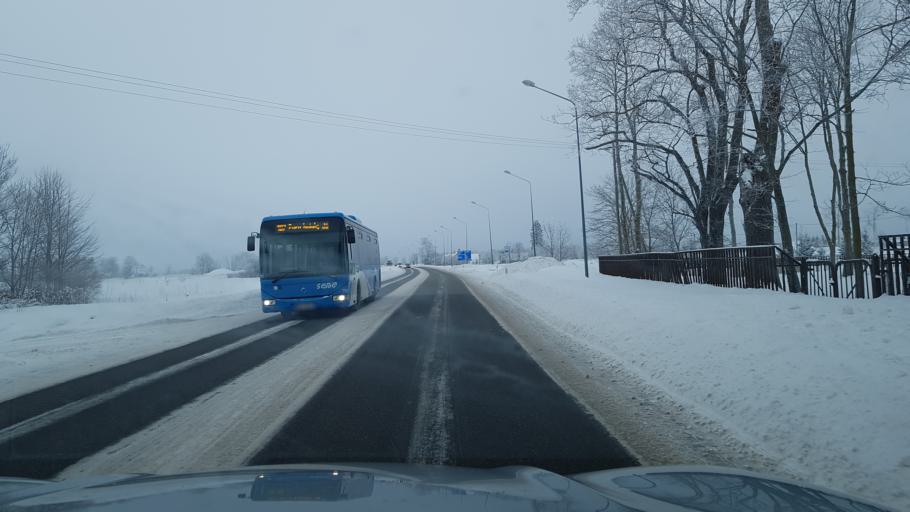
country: EE
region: Ida-Virumaa
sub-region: Johvi vald
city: Johvi
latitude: 59.3328
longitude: 27.4030
